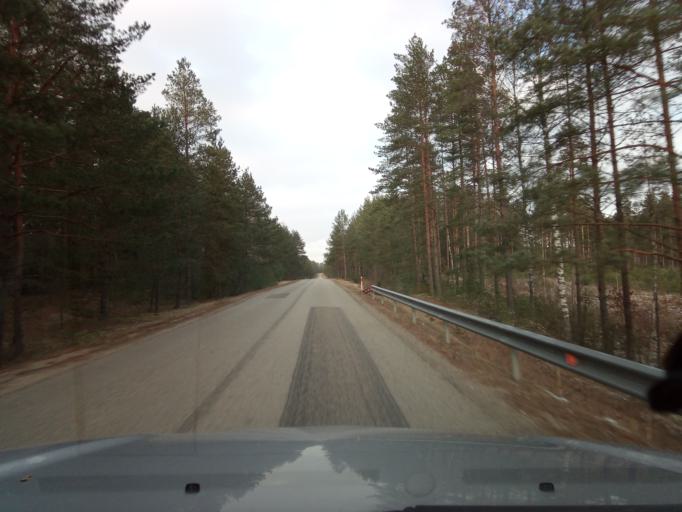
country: LT
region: Alytaus apskritis
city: Varena
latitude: 54.1885
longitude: 24.5218
